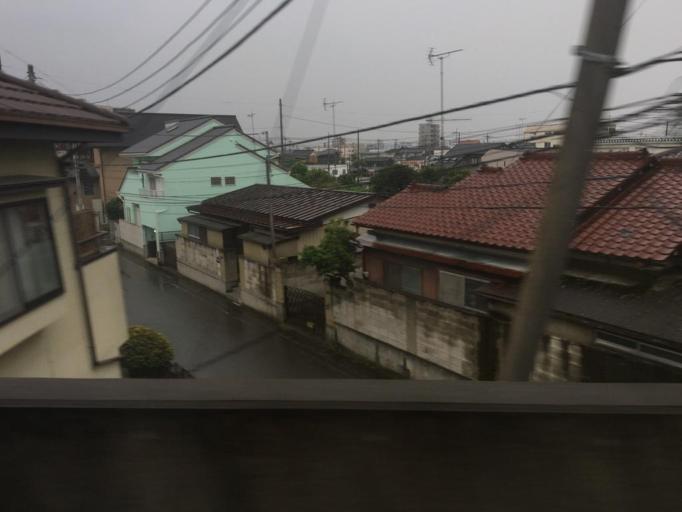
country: JP
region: Gunma
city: Ota
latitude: 36.2925
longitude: 139.3659
